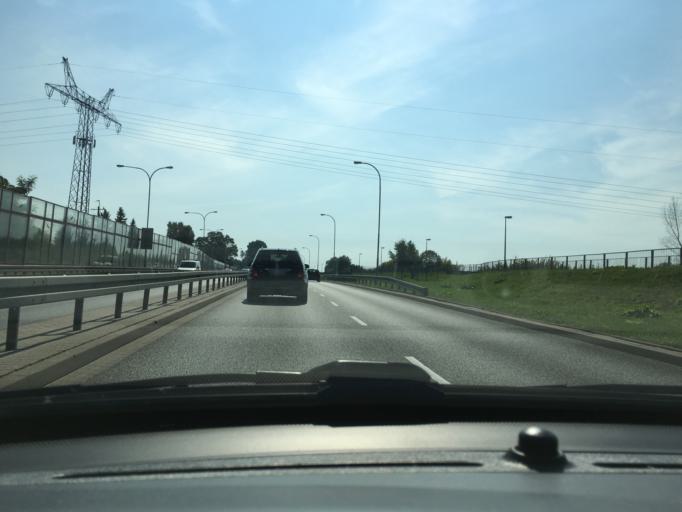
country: PL
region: Masovian Voivodeship
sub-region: Warszawa
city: Wilanow
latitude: 52.2027
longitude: 21.1151
